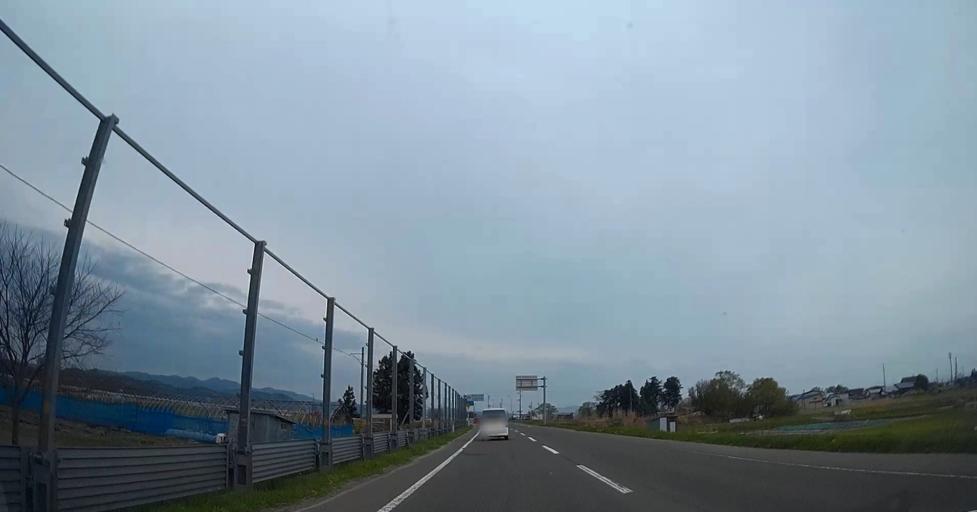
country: JP
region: Aomori
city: Aomori Shi
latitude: 40.9026
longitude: 140.6660
